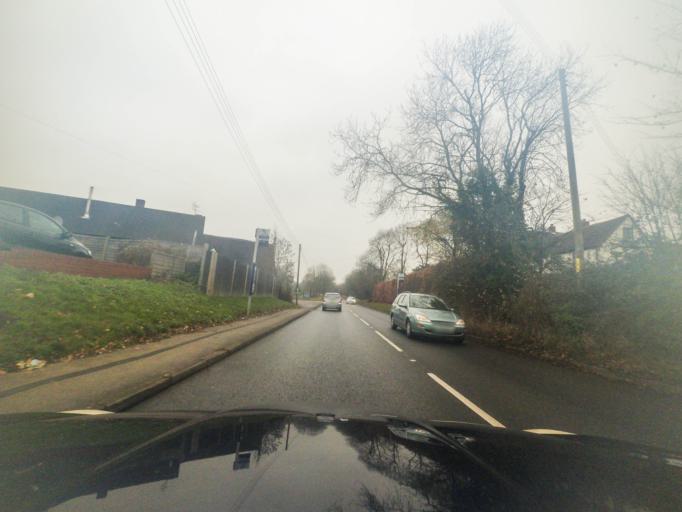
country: GB
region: England
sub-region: Solihull
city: Balsall Common
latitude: 52.3910
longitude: -1.6721
